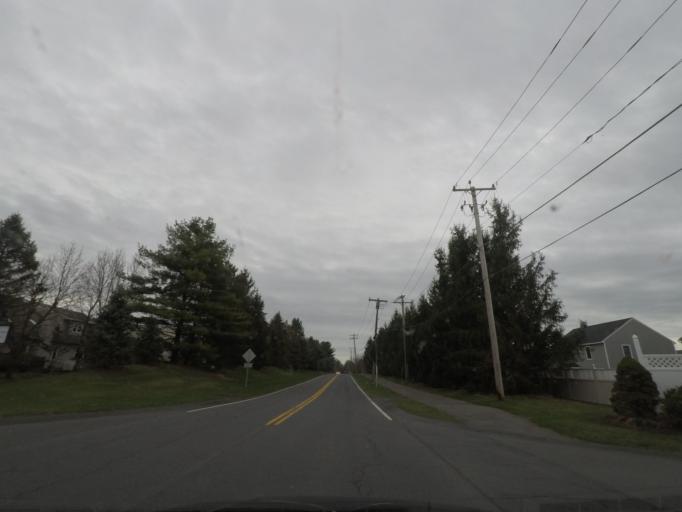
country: US
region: New York
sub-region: Albany County
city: Delmar
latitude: 42.5966
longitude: -73.8115
